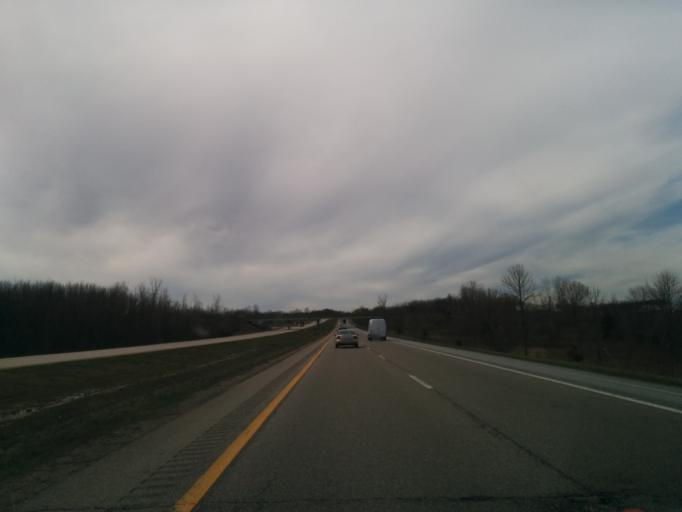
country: US
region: Michigan
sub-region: Ottawa County
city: Holland
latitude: 42.7461
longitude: -86.0688
